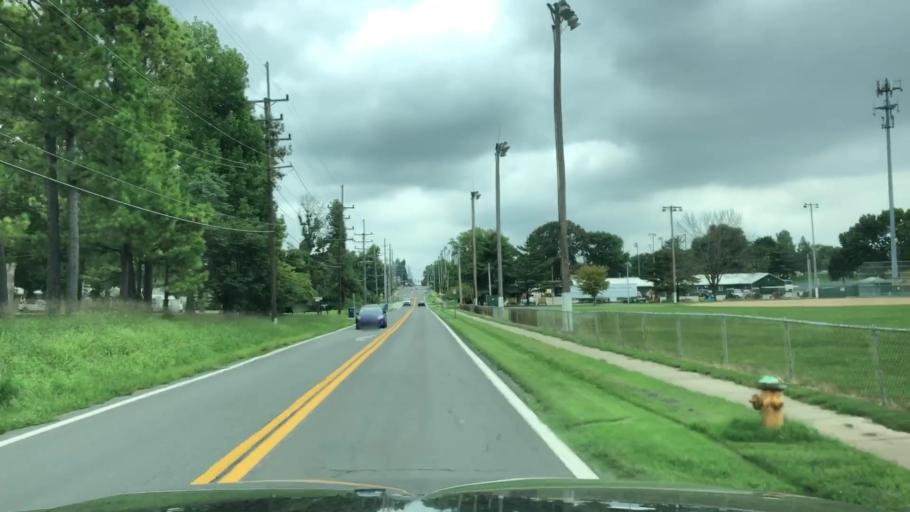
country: US
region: Missouri
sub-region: Saint Louis County
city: Hazelwood
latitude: 38.8120
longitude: -90.3639
